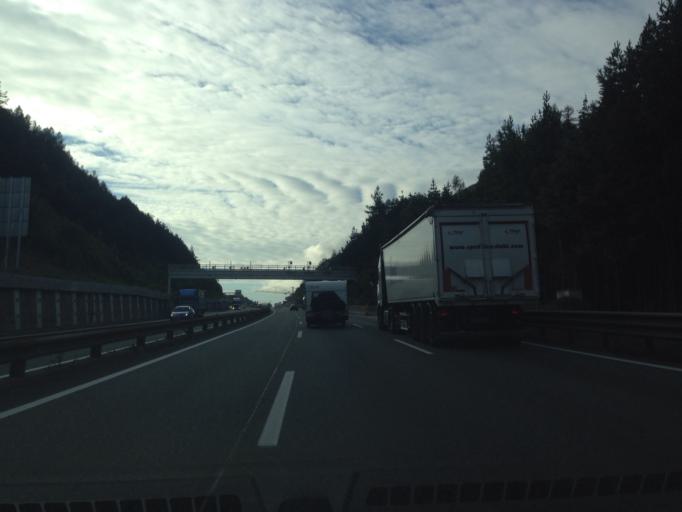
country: AT
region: Tyrol
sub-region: Politischer Bezirk Innsbruck Land
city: Mutters
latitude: 47.2203
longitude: 11.3931
